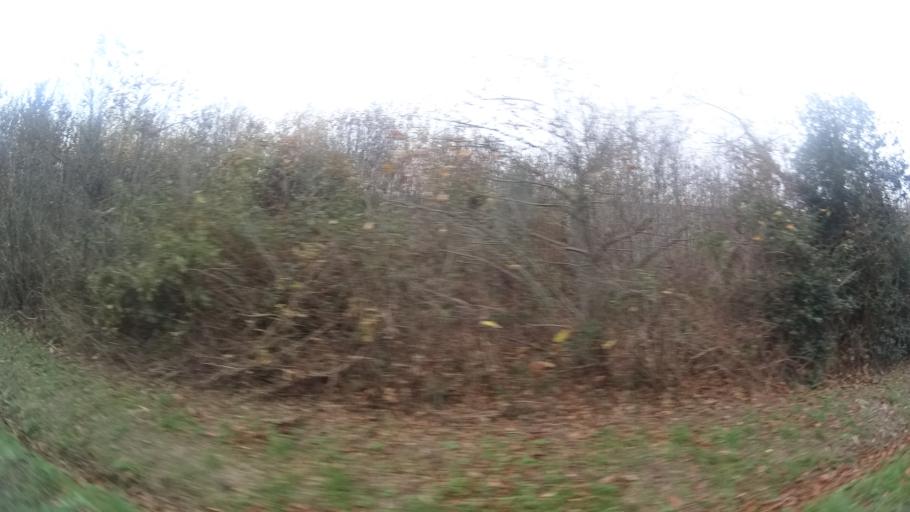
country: FR
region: Brittany
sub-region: Departement d'Ille-et-Vilaine
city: Bains-sur-Oust
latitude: 47.6828
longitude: -2.0477
